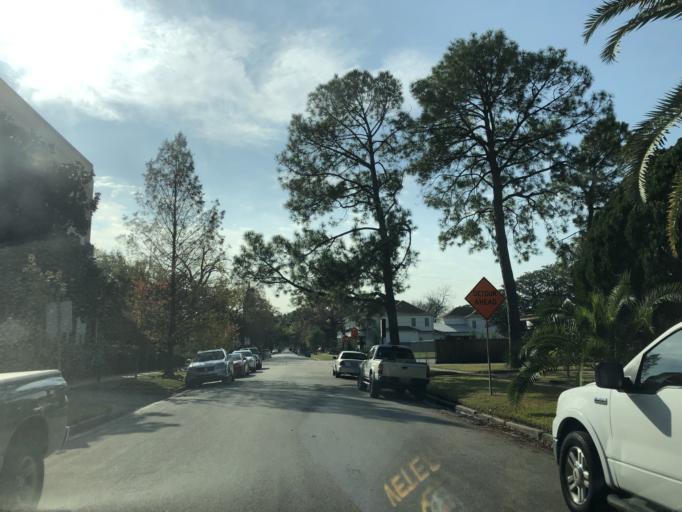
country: US
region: Texas
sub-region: Harris County
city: Houston
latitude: 29.7915
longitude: -95.3964
